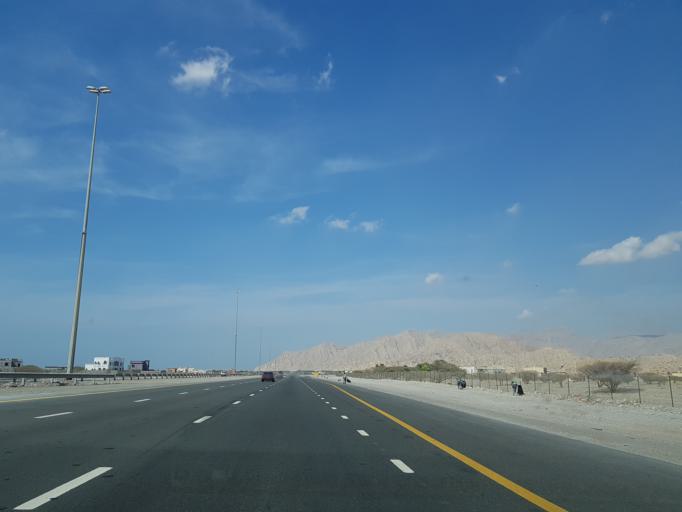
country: AE
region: Ra's al Khaymah
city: Ras al-Khaimah
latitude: 25.7915
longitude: 56.0314
